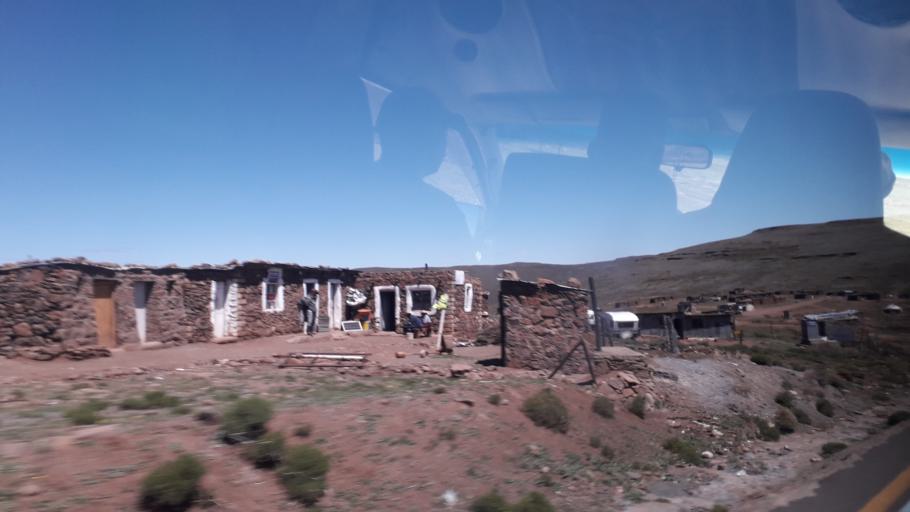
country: LS
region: Mokhotlong
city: Mokhotlong
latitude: -29.0145
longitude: 28.8447
